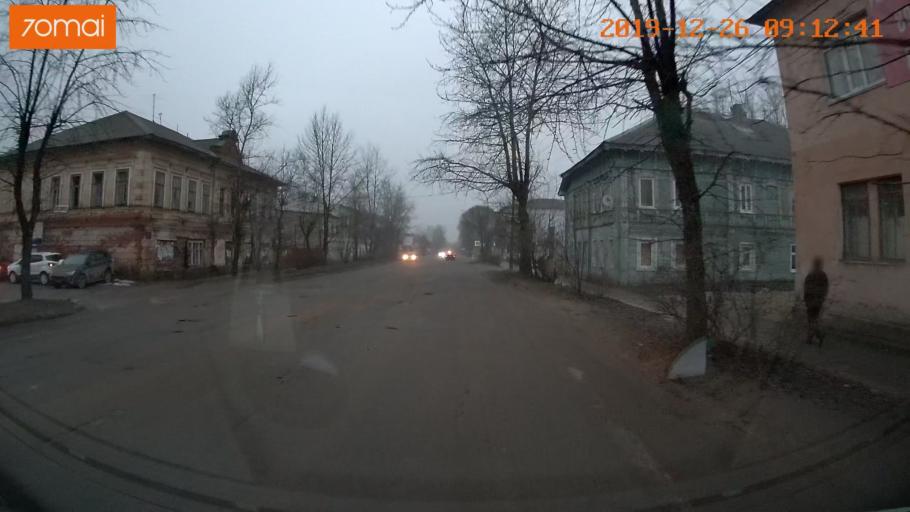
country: RU
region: Vologda
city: Gryazovets
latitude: 58.8824
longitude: 40.2536
